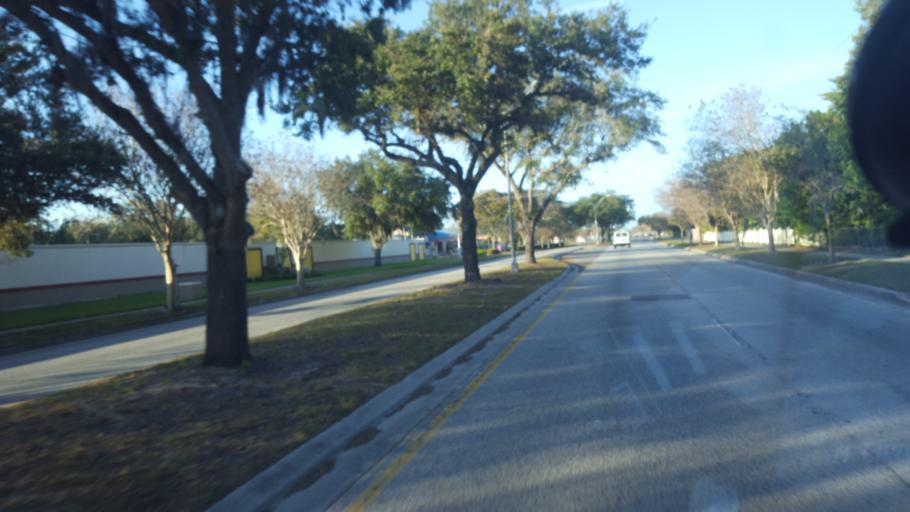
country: US
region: Florida
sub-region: Sarasota County
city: Kensington Park
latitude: 27.3328
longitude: -82.4976
